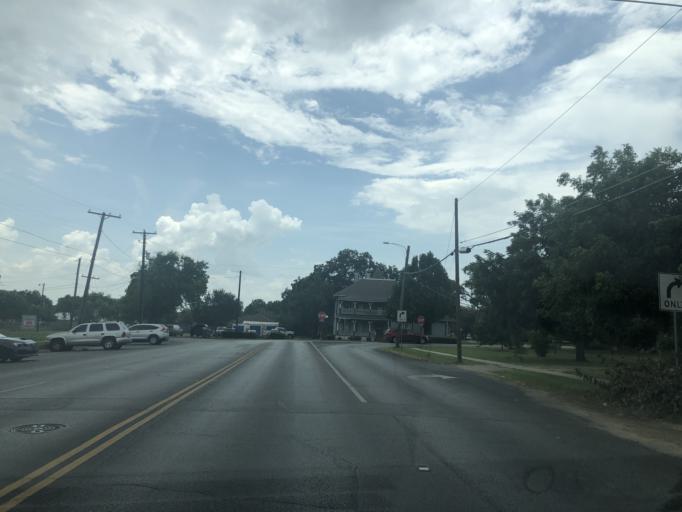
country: US
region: Texas
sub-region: Dallas County
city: Grand Prairie
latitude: 32.7429
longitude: -97.0034
